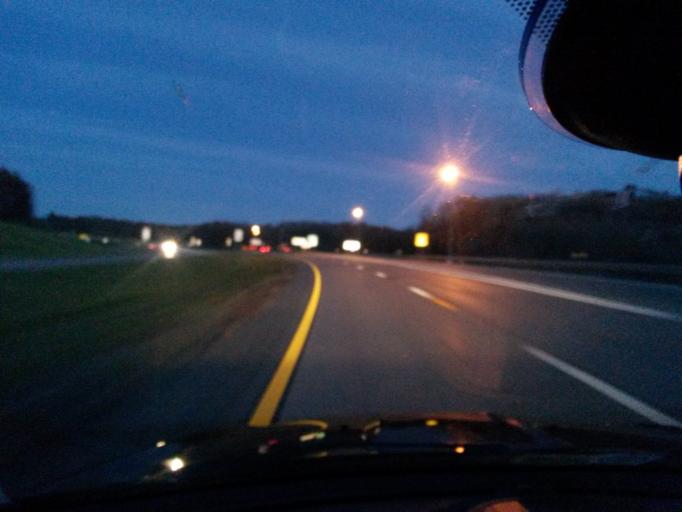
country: US
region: West Virginia
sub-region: Raleigh County
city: Shady Spring
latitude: 37.7671
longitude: -80.9896
